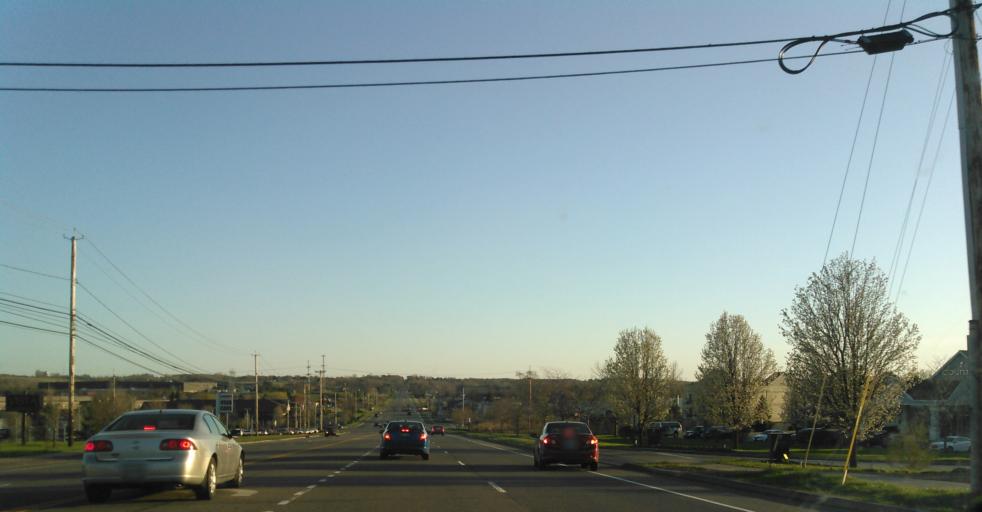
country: US
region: New York
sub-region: Monroe County
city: Rochester
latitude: 43.0611
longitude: -77.6509
